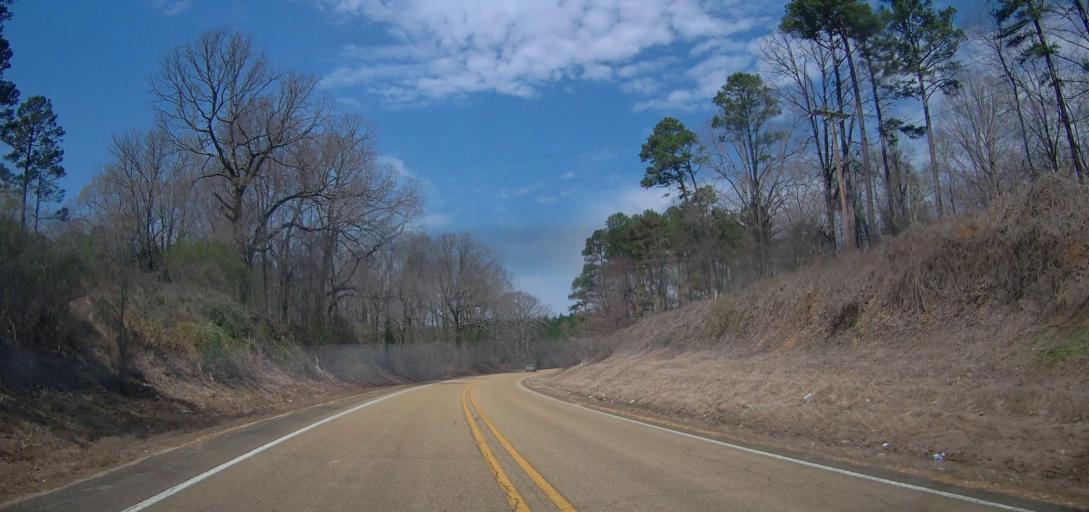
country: US
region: Mississippi
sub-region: Union County
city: New Albany
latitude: 34.6040
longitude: -89.1460
